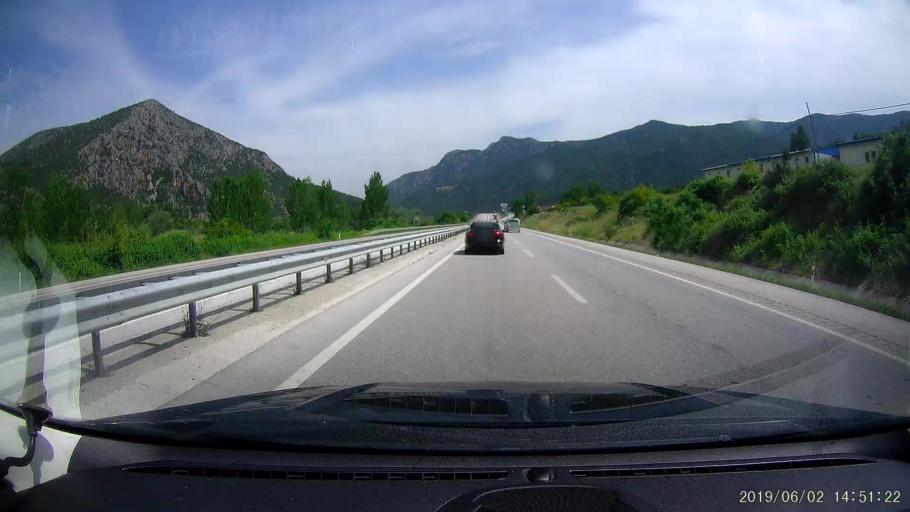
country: TR
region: Corum
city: Kargi
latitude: 41.0610
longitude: 34.5391
